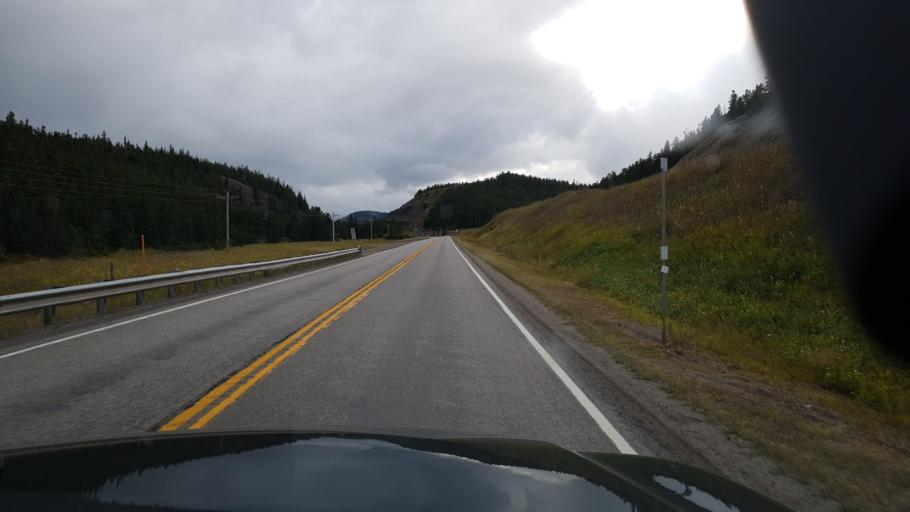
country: US
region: Montana
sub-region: Glacier County
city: South Browning
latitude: 48.3335
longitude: -113.3337
